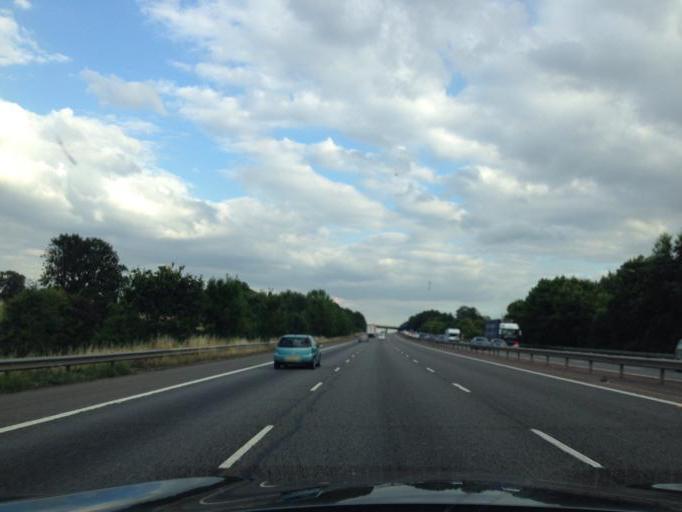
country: GB
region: England
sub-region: Oxfordshire
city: Hanwell
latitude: 52.0934
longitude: -1.3435
